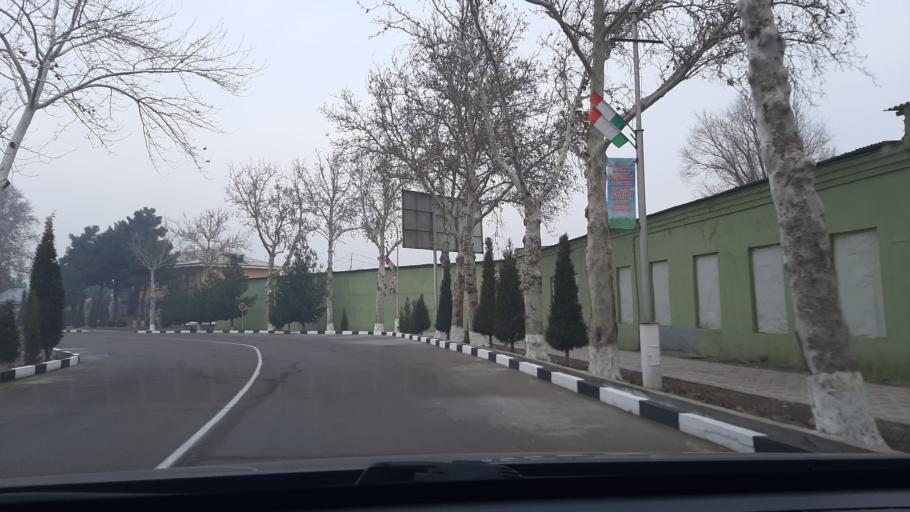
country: TJ
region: Viloyati Sughd
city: Chkalov
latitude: 40.2388
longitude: 69.7011
